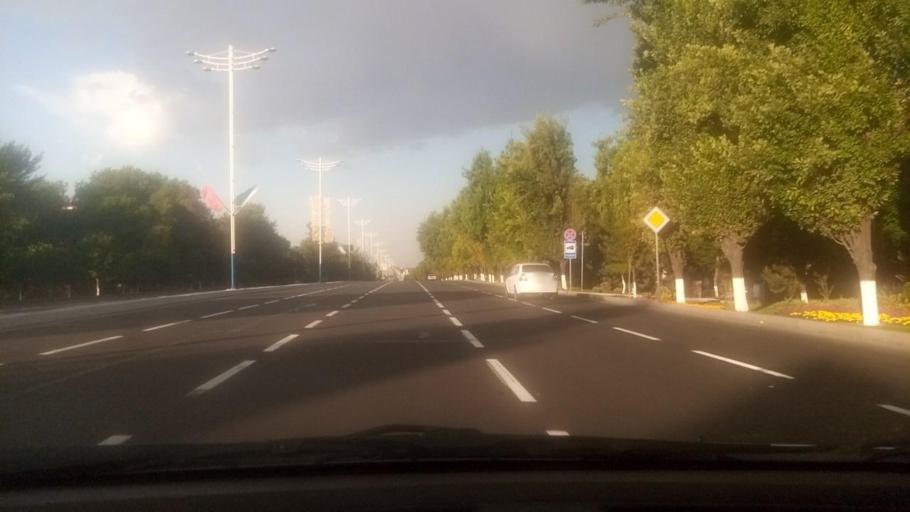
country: UZ
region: Toshkent
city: Salor
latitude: 41.3317
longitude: 69.3320
